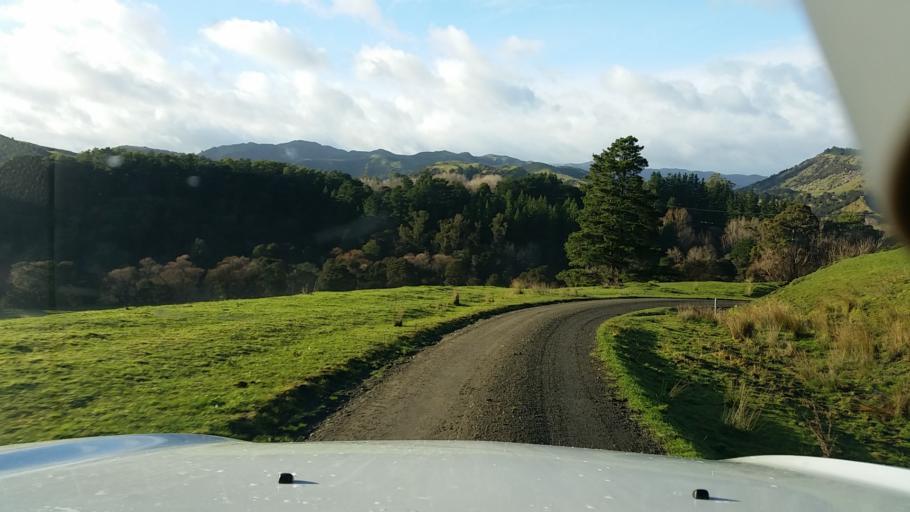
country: NZ
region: Wellington
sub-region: South Wairarapa District
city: Waipawa
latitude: -41.2640
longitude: 175.6849
